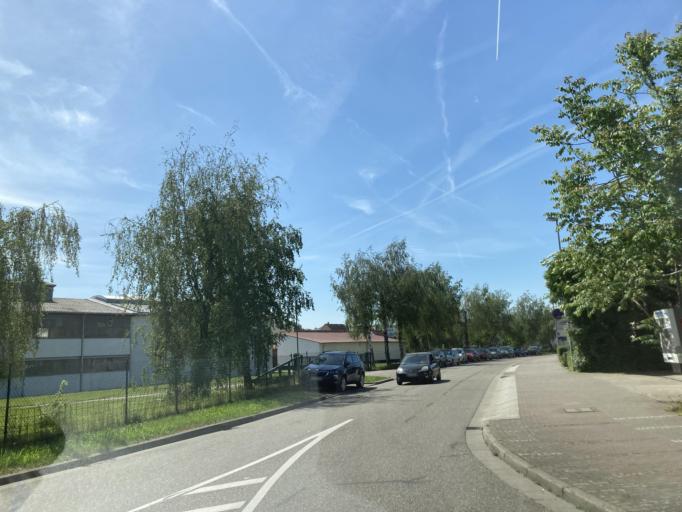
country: DE
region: Baden-Wuerttemberg
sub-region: Karlsruhe Region
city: Bruchsal
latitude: 49.1306
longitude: 8.5873
